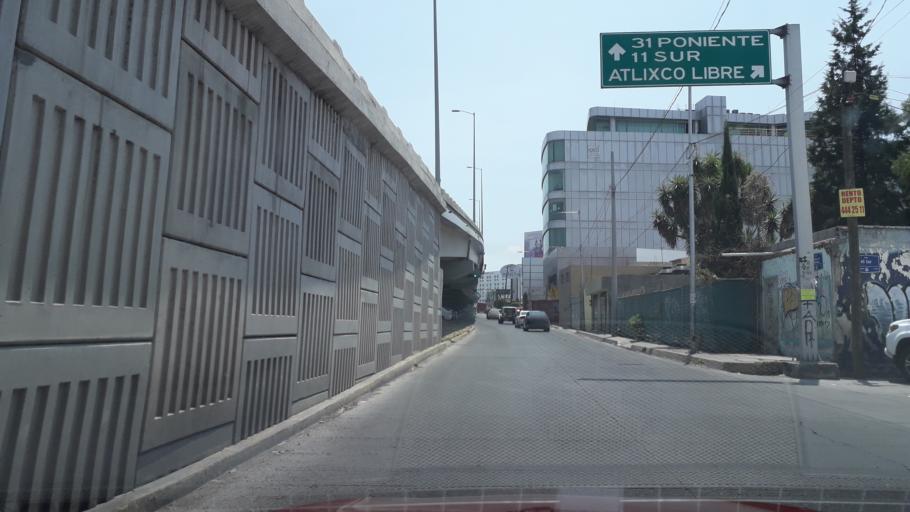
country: MX
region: Puebla
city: Puebla
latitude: 19.0490
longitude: -98.2379
